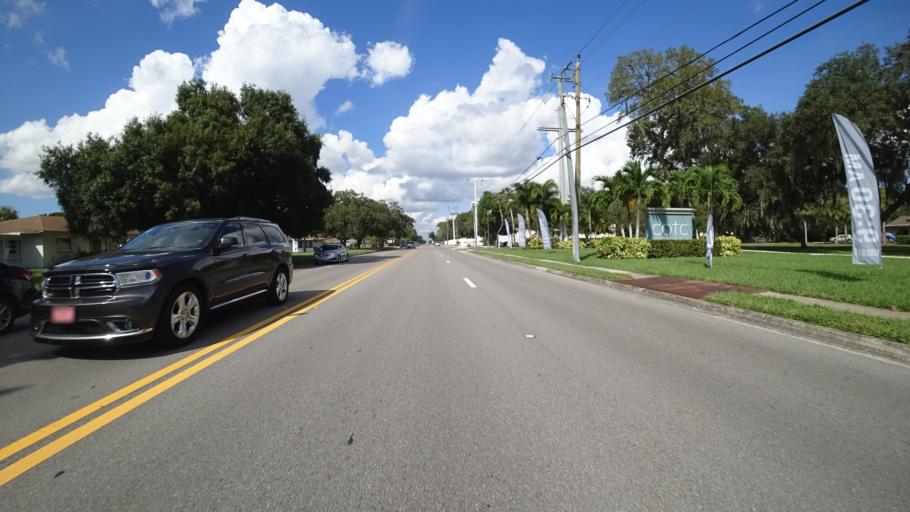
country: US
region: Florida
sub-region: Manatee County
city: South Bradenton
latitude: 27.4517
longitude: -82.5876
